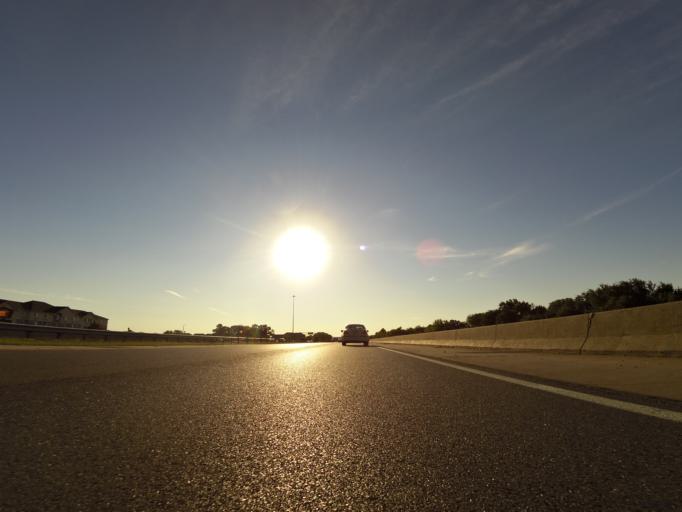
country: US
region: Kansas
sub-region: Sedgwick County
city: Bellaire
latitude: 37.7455
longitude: -97.2797
